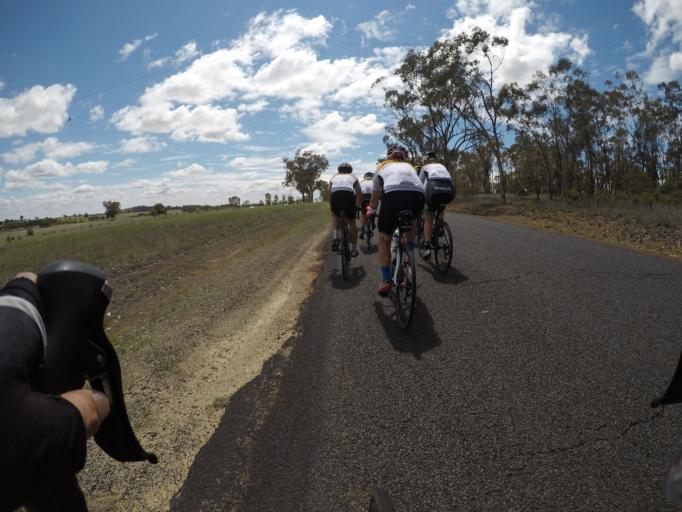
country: AU
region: New South Wales
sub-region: Dubbo Municipality
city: Dubbo
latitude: -32.3735
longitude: 148.5799
